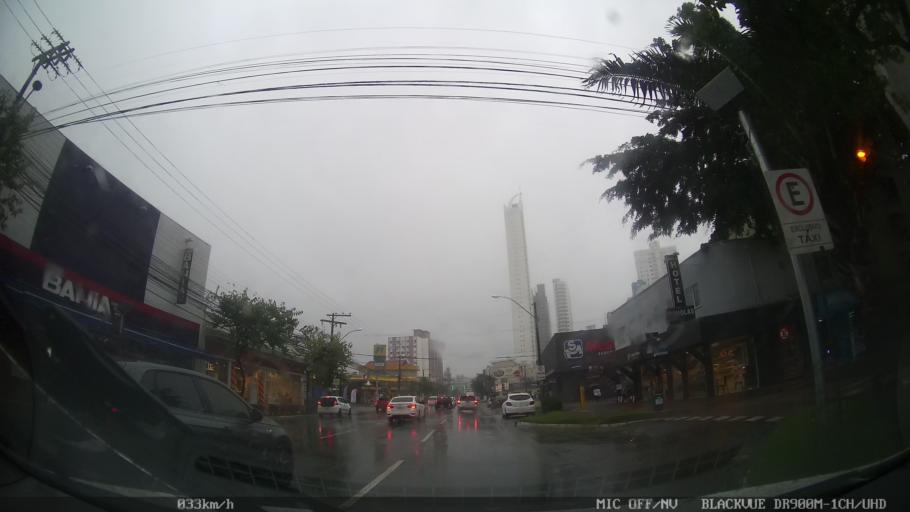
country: BR
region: Santa Catarina
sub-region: Balneario Camboriu
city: Balneario Camboriu
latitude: -26.9829
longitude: -48.6401
